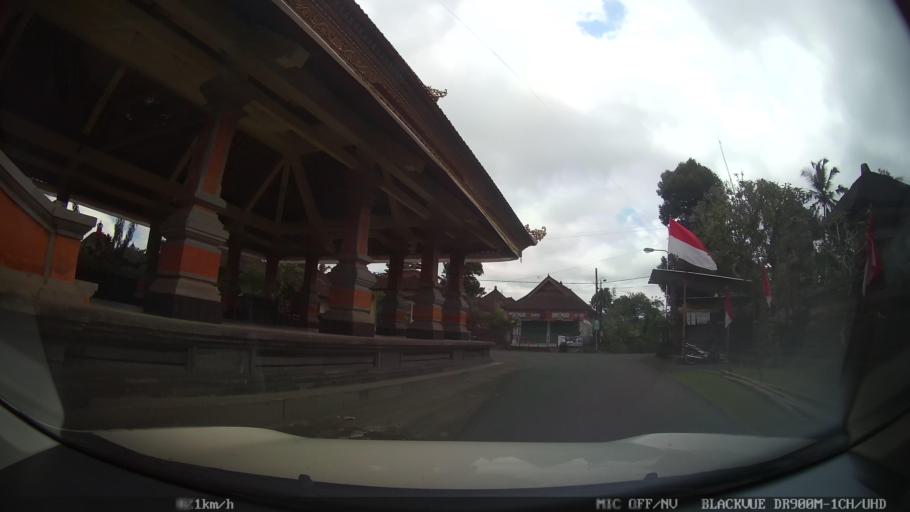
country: ID
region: Bali
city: Banjar Susut Kaja
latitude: -8.4423
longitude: 115.3340
